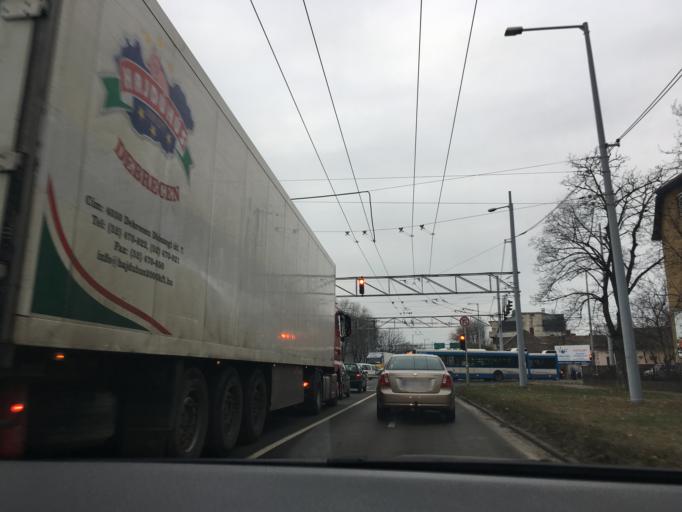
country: HU
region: Hajdu-Bihar
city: Debrecen
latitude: 47.5305
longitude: 21.6394
